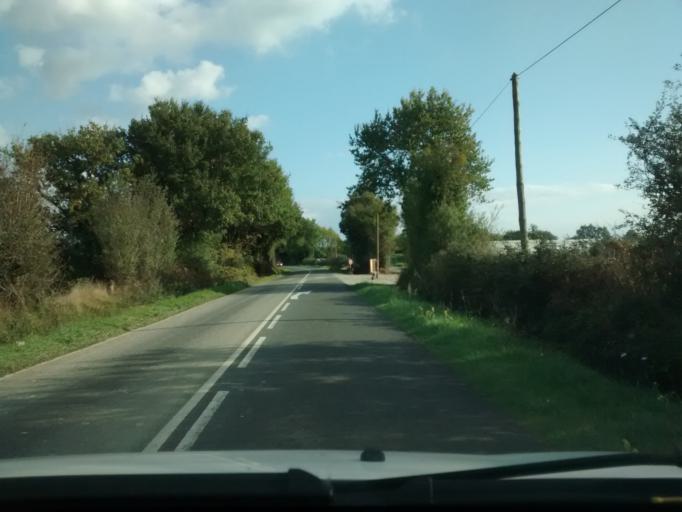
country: FR
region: Pays de la Loire
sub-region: Departement de la Loire-Atlantique
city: Sautron
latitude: 47.2854
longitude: -1.6530
